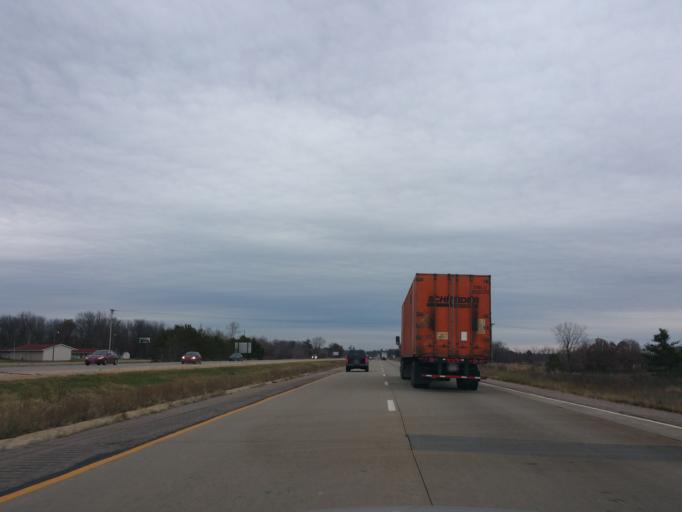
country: US
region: Wisconsin
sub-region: Juneau County
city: New Lisbon
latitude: 43.8805
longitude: -90.1427
